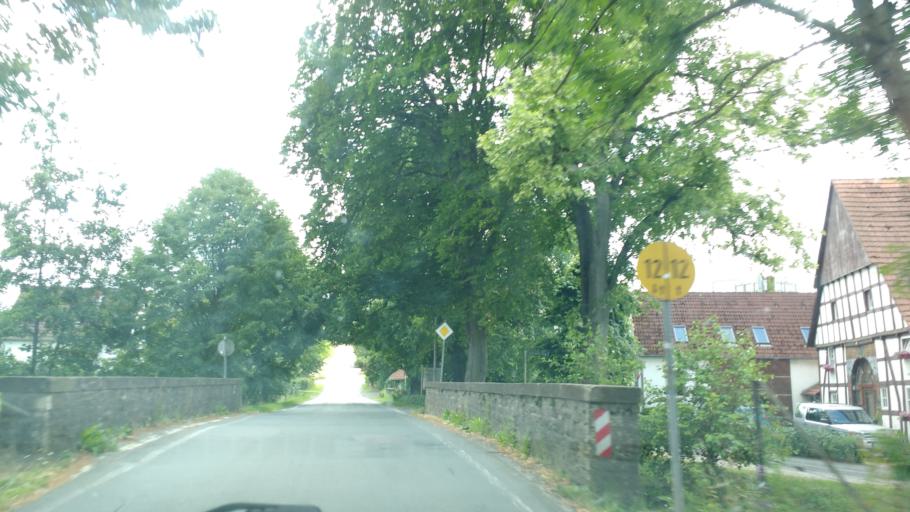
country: DE
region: North Rhine-Westphalia
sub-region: Regierungsbezirk Detmold
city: Detmold
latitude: 51.9059
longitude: 8.8972
